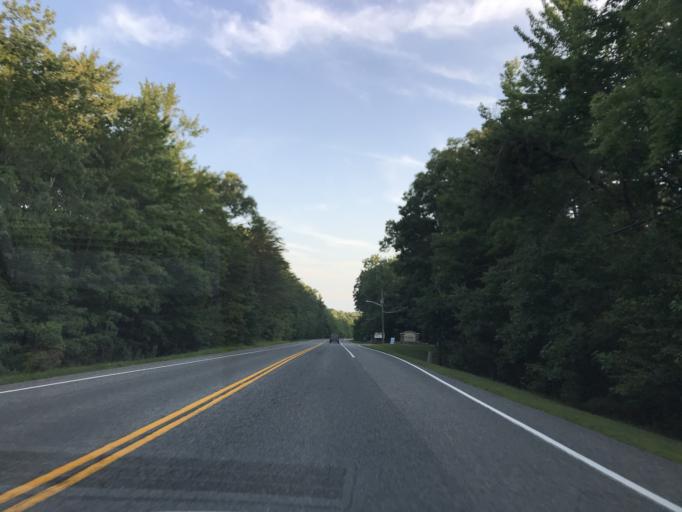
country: US
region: Maryland
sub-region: Cecil County
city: Charlestown
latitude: 39.5479
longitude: -75.9480
